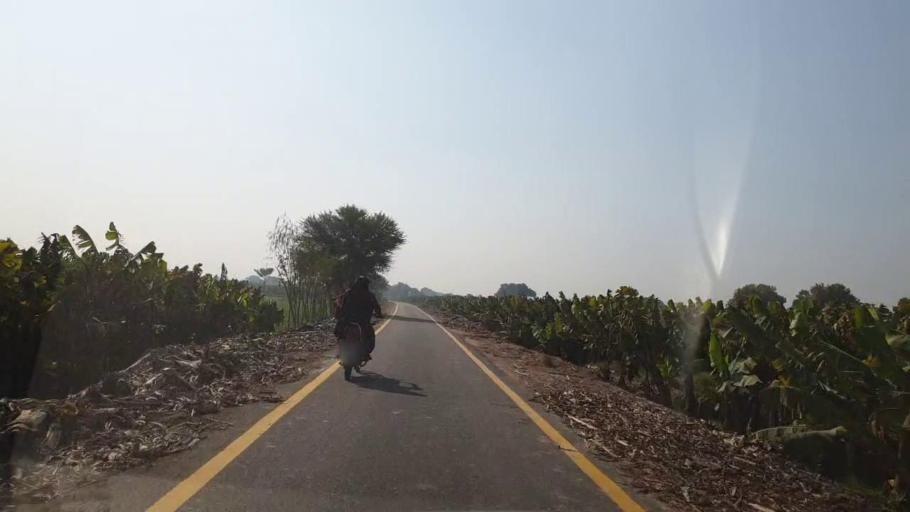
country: PK
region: Sindh
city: Matiari
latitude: 25.5350
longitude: 68.4929
